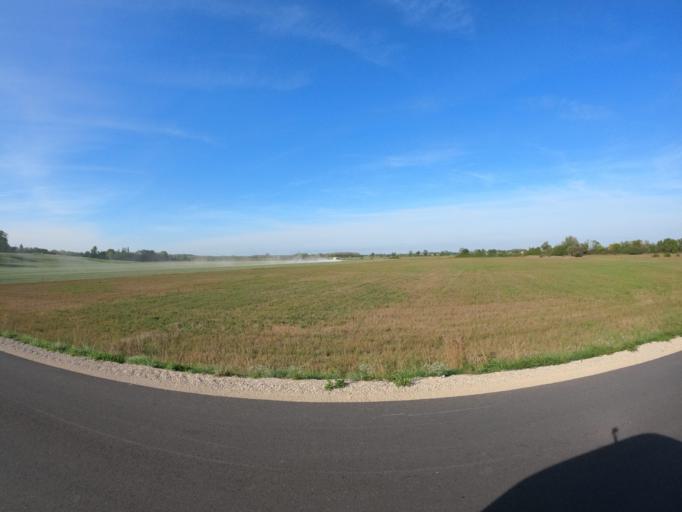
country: FR
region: Franche-Comte
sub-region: Departement du Jura
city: Bletterans
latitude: 46.7357
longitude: 5.5026
